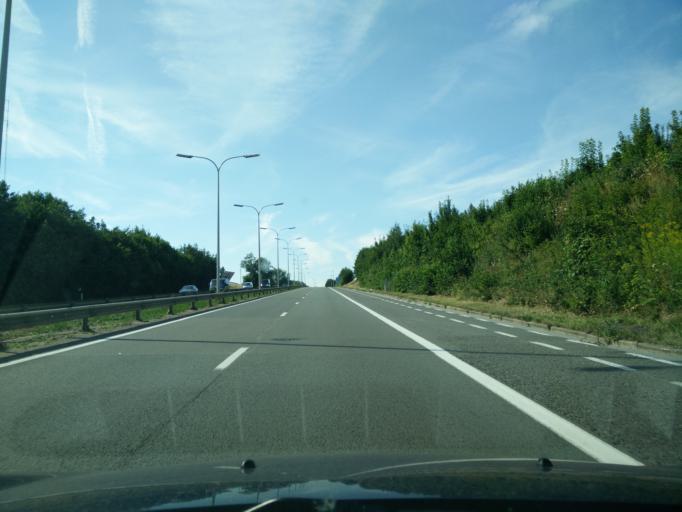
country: BE
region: Flanders
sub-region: Provincie Oost-Vlaanderen
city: Ninove
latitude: 50.8423
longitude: 4.0347
